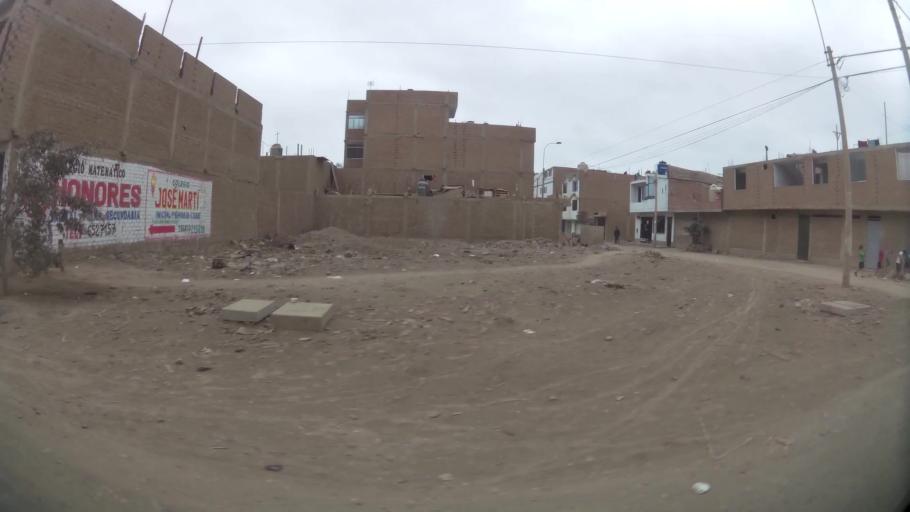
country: PE
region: Lima
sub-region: Lima
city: Independencia
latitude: -11.9579
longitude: -77.0940
